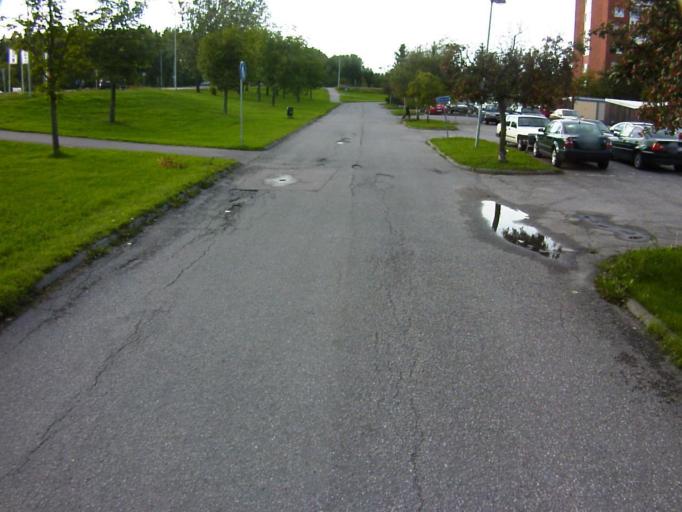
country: SE
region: Soedermanland
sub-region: Eskilstuna Kommun
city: Eskilstuna
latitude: 59.3901
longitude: 16.5341
